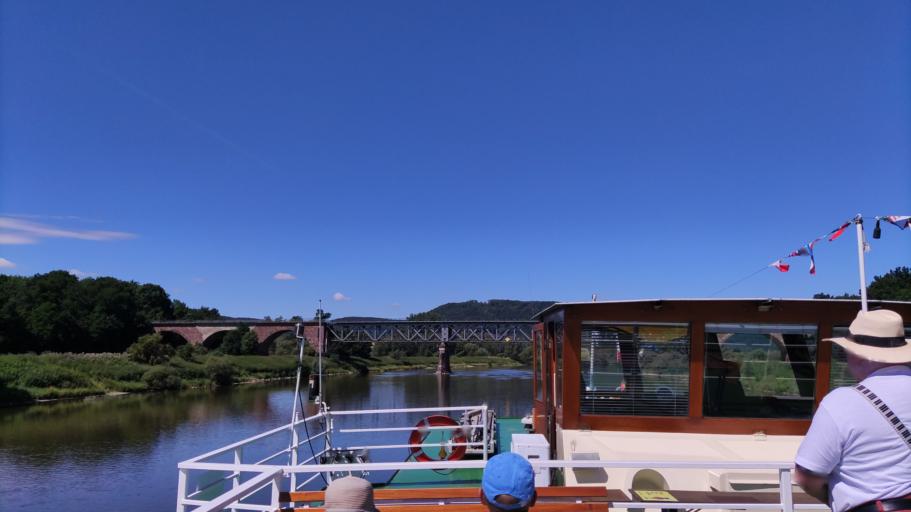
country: DE
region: Lower Saxony
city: Boffzen
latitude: 51.7357
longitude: 9.3855
